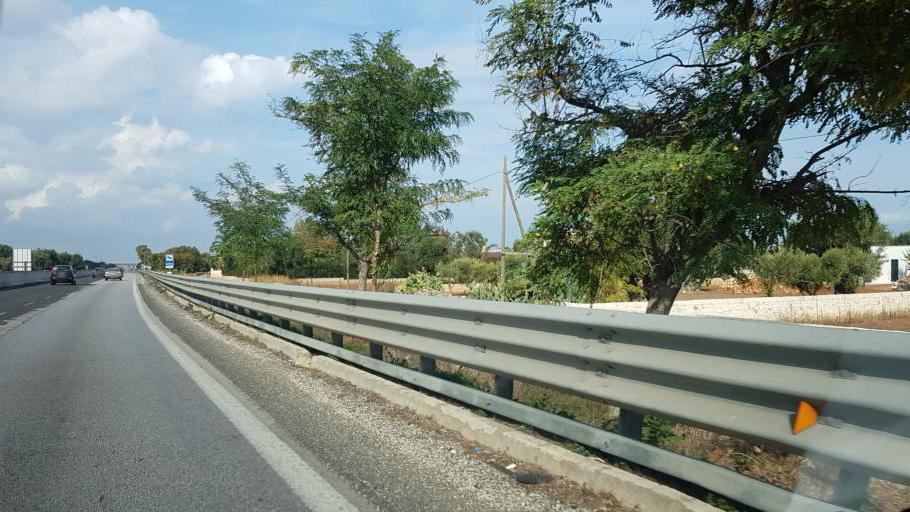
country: IT
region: Apulia
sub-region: Provincia di Brindisi
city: Fasano
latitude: 40.8435
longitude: 17.3655
